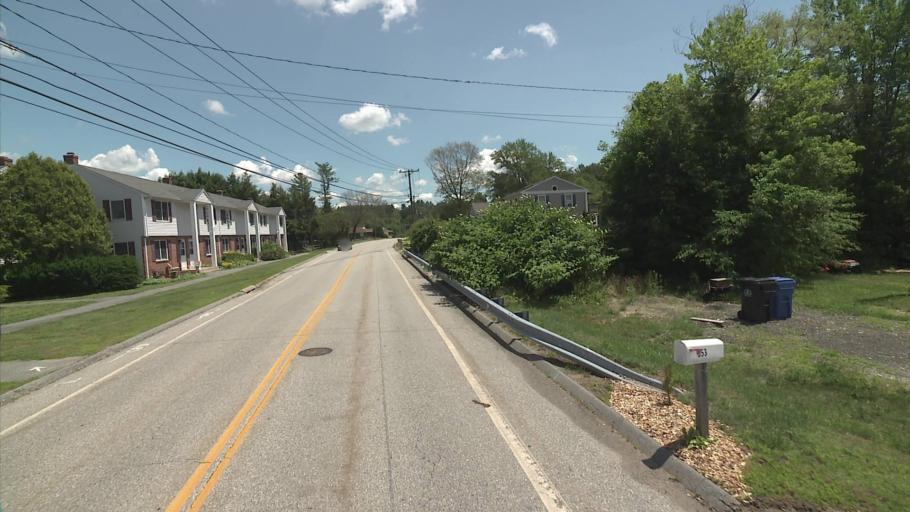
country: US
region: Connecticut
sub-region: New London County
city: Jewett City
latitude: 41.6131
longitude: -71.9679
